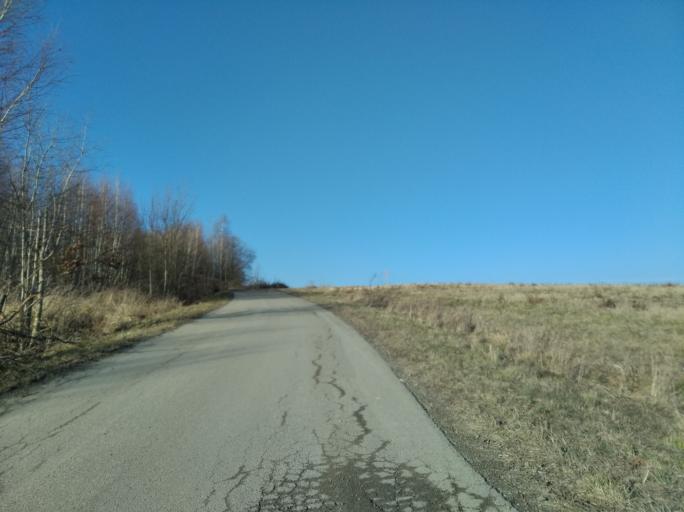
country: PL
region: Subcarpathian Voivodeship
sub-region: Powiat strzyzowski
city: Jawornik
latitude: 49.8287
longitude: 21.8706
